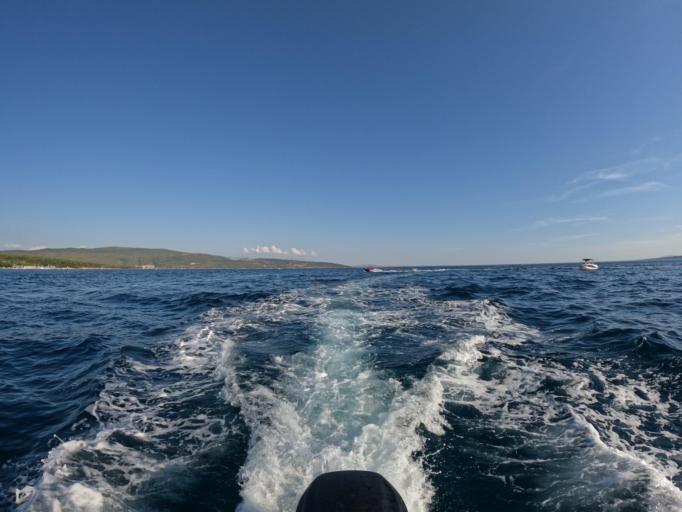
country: HR
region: Primorsko-Goranska
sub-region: Grad Krk
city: Krk
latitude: 45.0218
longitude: 14.5792
